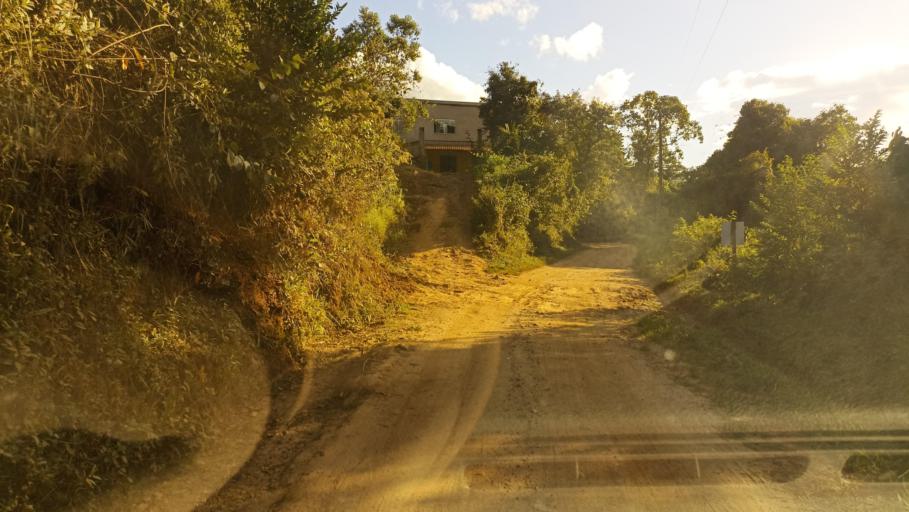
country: BR
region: Minas Gerais
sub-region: Ouro Preto
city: Ouro Preto
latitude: -20.3077
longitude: -43.5772
